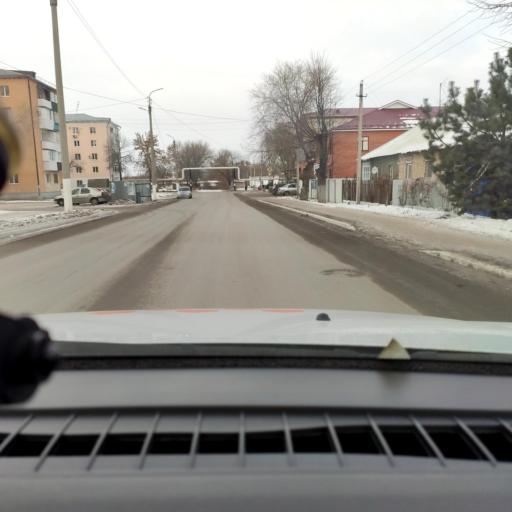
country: RU
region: Samara
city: Chapayevsk
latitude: 52.9602
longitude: 49.6878
